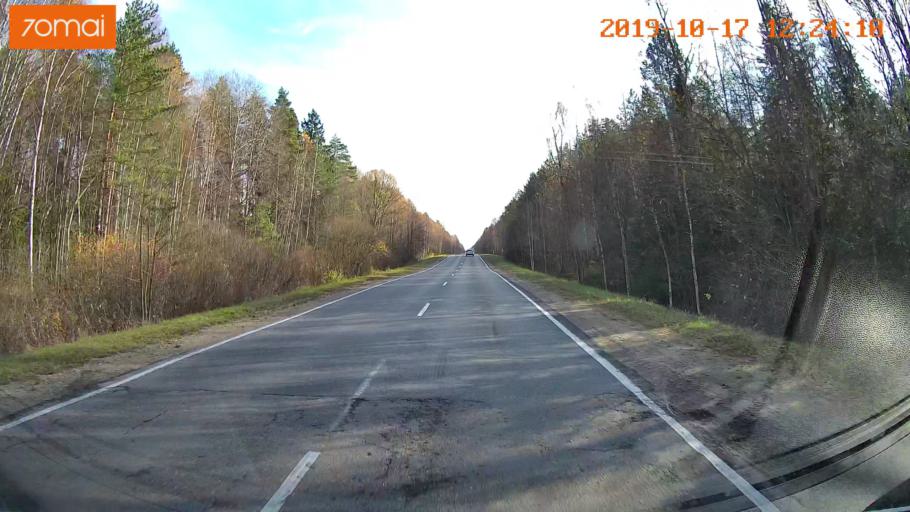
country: RU
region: Rjazan
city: Gus'-Zheleznyy
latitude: 55.0377
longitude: 41.2093
